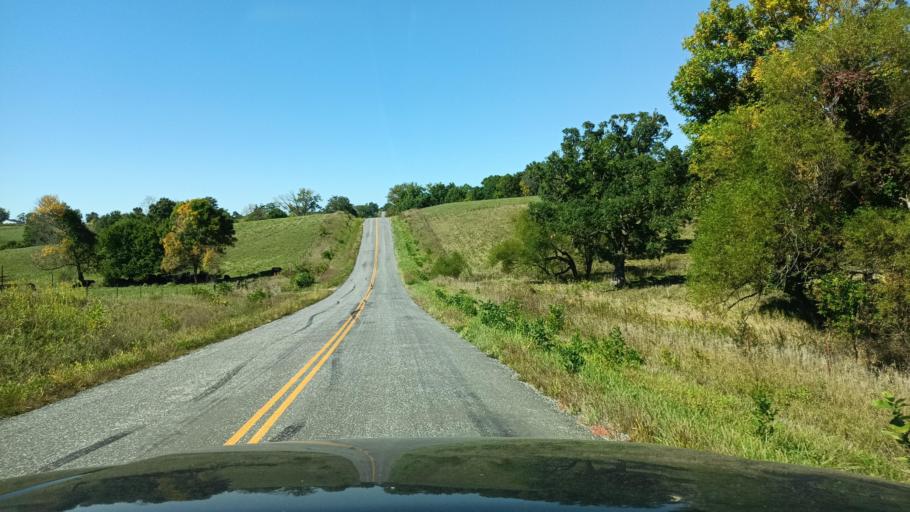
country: US
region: Missouri
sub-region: Adair County
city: Kirksville
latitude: 40.3301
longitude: -92.5449
